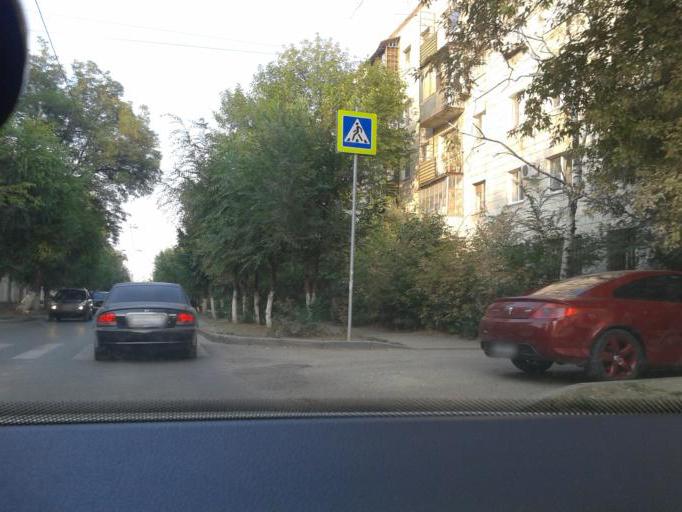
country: RU
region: Volgograd
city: Volgograd
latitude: 48.6972
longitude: 44.5048
